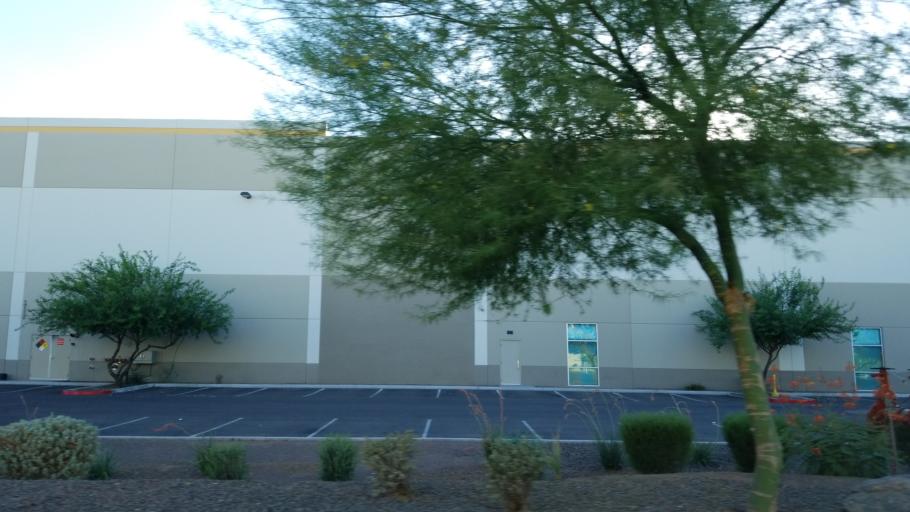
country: US
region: Arizona
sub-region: Maricopa County
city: Laveen
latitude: 33.4214
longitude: -112.1780
